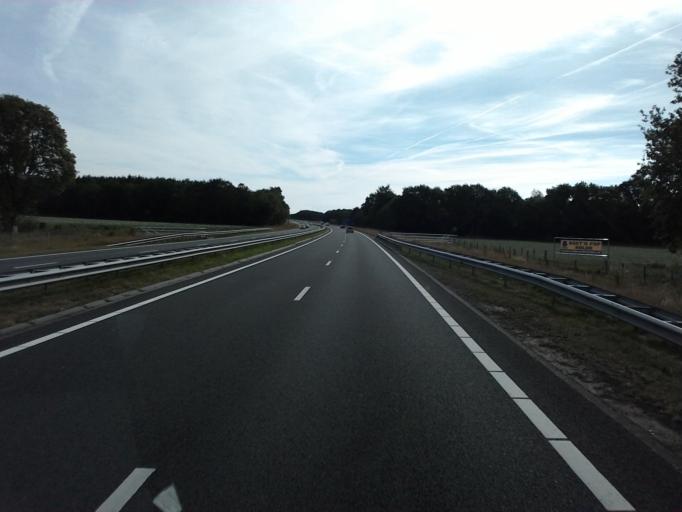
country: NL
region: Drenthe
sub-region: Gemeente Assen
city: Assen
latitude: 52.9720
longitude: 6.6389
